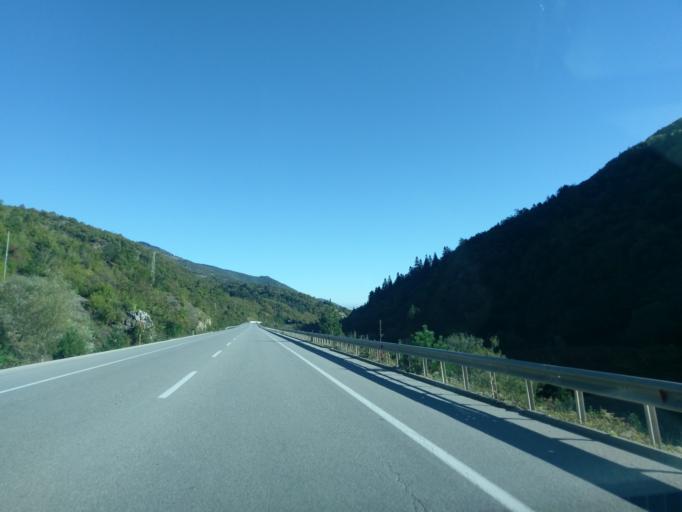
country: TR
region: Sinop
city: Erfelek
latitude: 41.7172
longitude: 34.9356
